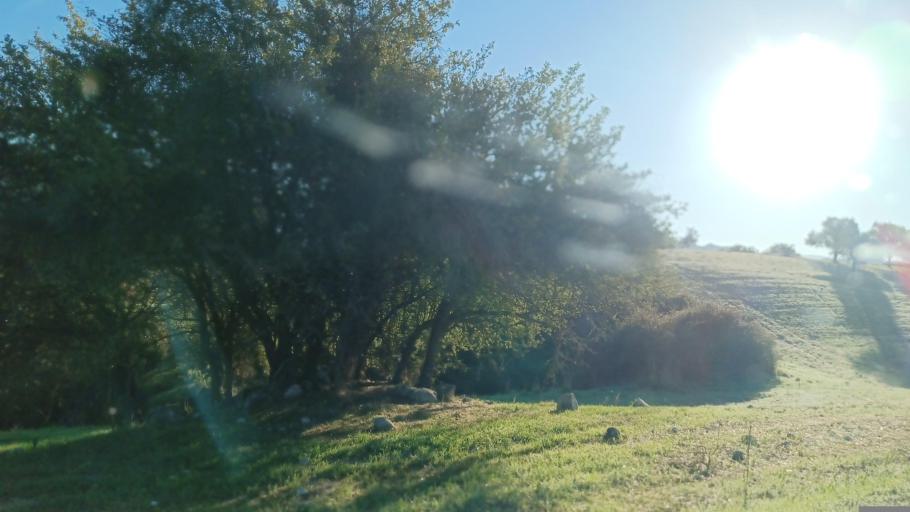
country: CY
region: Pafos
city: Polis
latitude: 34.9557
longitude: 32.5455
